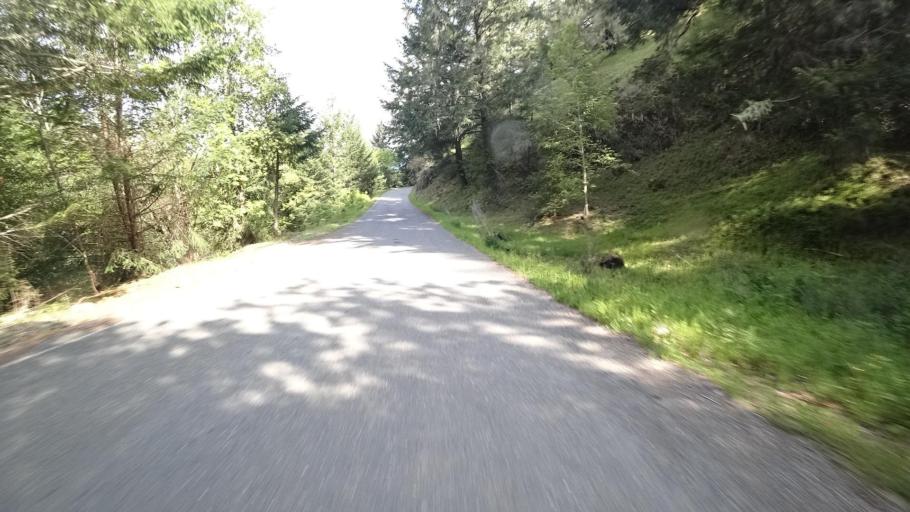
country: US
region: California
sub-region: Humboldt County
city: Redway
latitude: 40.1626
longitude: -123.5608
